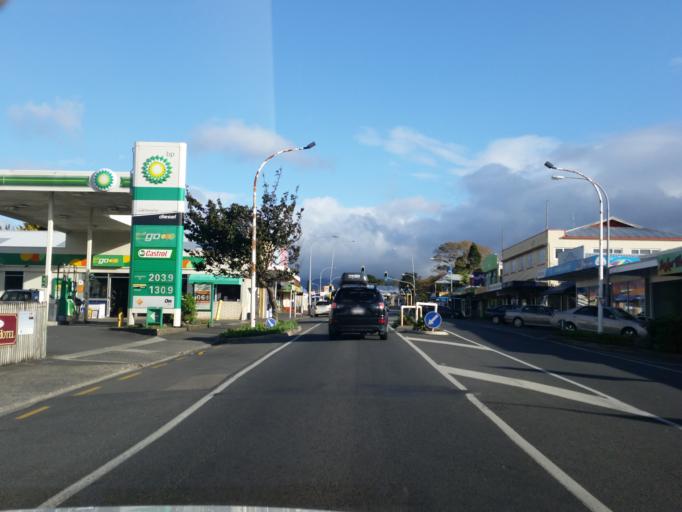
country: NZ
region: Bay of Plenty
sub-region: Western Bay of Plenty District
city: Katikati
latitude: -37.5521
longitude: 175.9180
